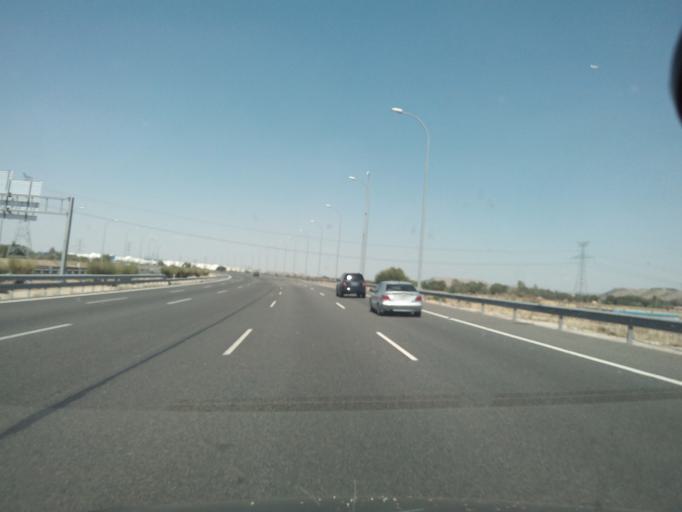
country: ES
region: Madrid
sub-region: Provincia de Madrid
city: San Fernando de Henares
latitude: 40.4138
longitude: -3.5048
